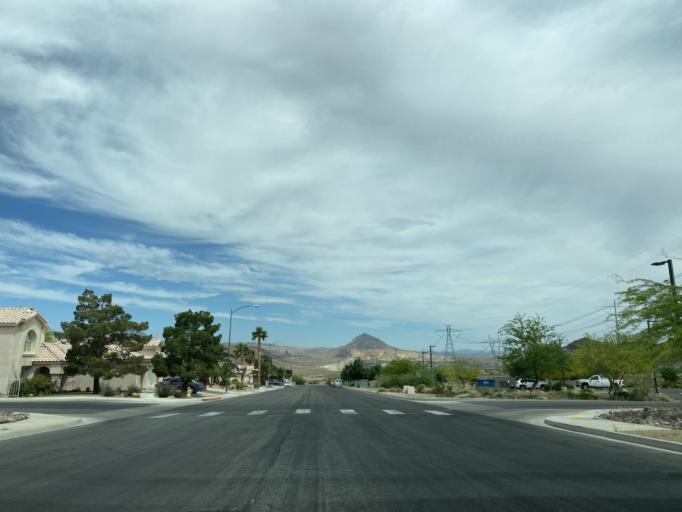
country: US
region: Nevada
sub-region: Clark County
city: Henderson
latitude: 36.0786
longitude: -114.9396
